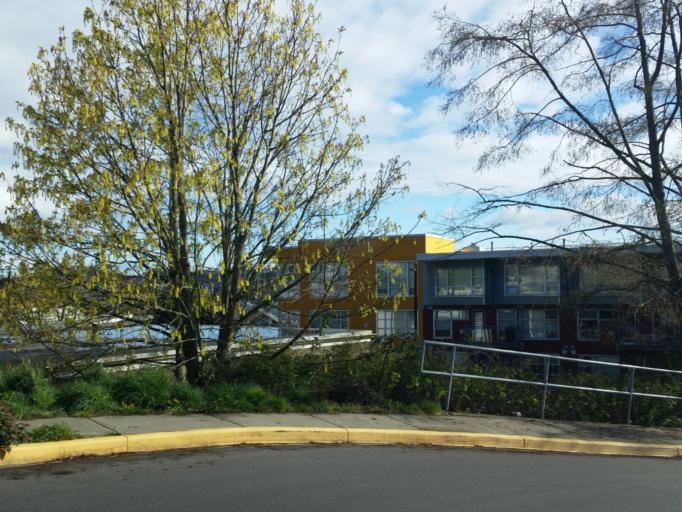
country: CA
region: British Columbia
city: Victoria
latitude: 48.4365
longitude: -123.3833
